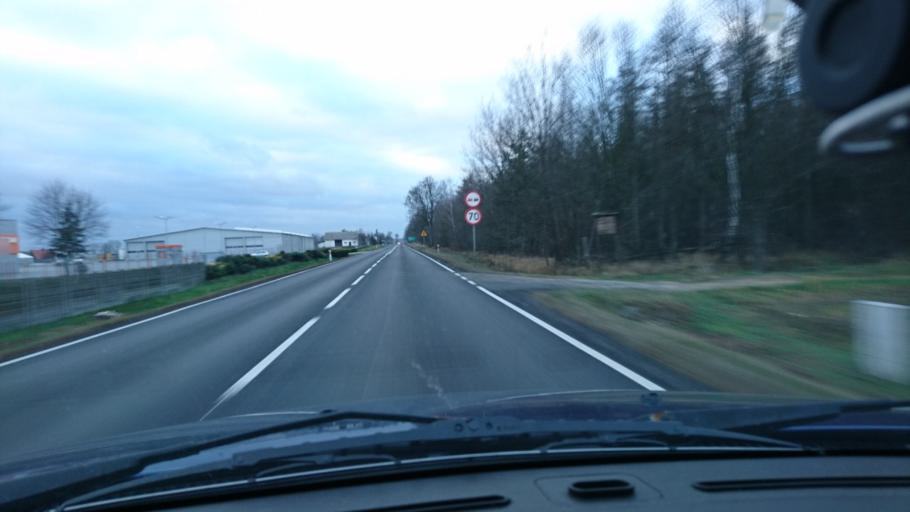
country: PL
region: Greater Poland Voivodeship
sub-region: Powiat kepinski
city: Leka Opatowska
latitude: 51.2247
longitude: 18.1000
